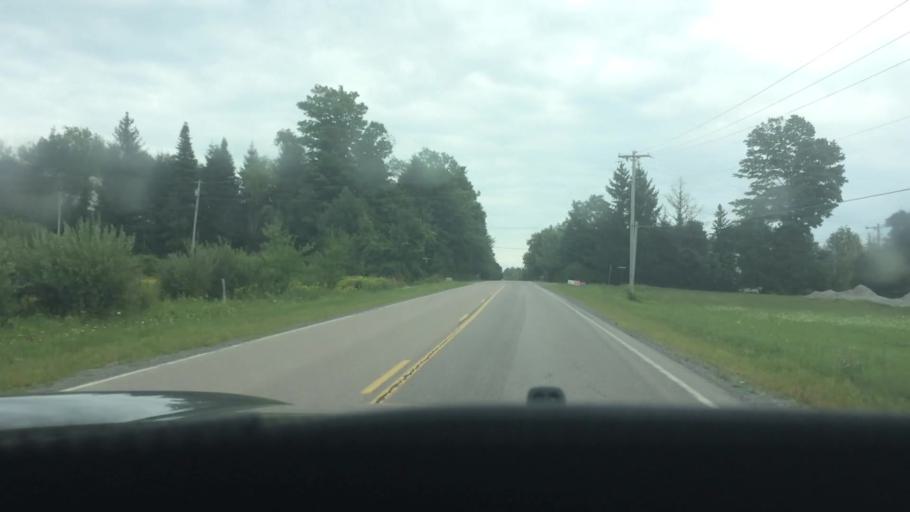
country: US
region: New York
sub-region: St. Lawrence County
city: Hannawa Falls
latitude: 44.5381
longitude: -75.0549
